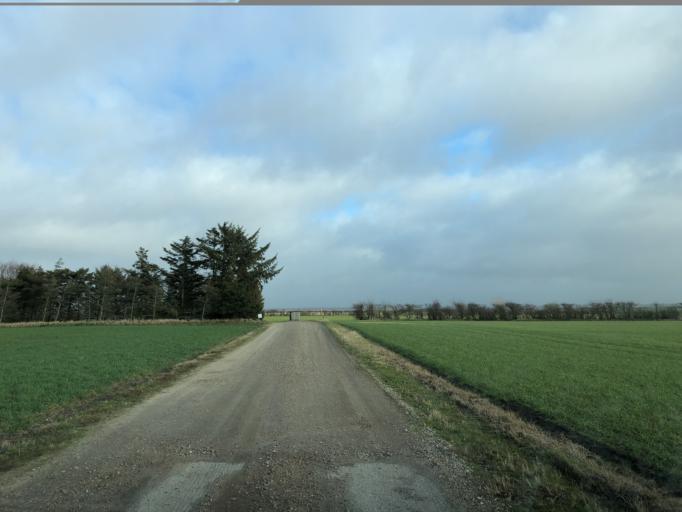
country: DK
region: Central Jutland
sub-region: Holstebro Kommune
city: Ulfborg
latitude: 56.3100
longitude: 8.2225
